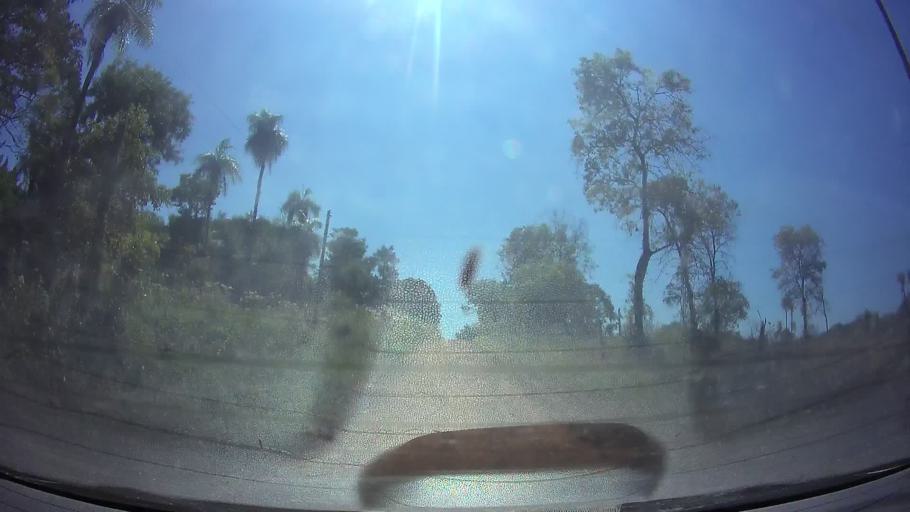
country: PY
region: Central
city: Limpio
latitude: -25.2416
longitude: -57.4436
